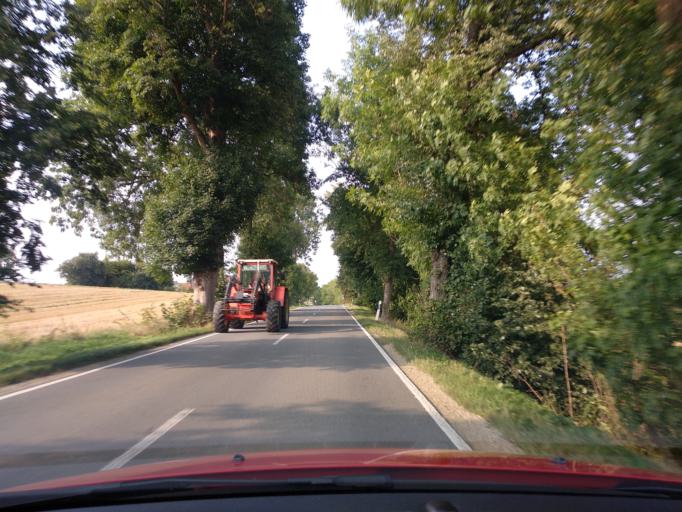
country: DE
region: Hesse
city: Liebenau
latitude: 51.4546
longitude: 9.3081
